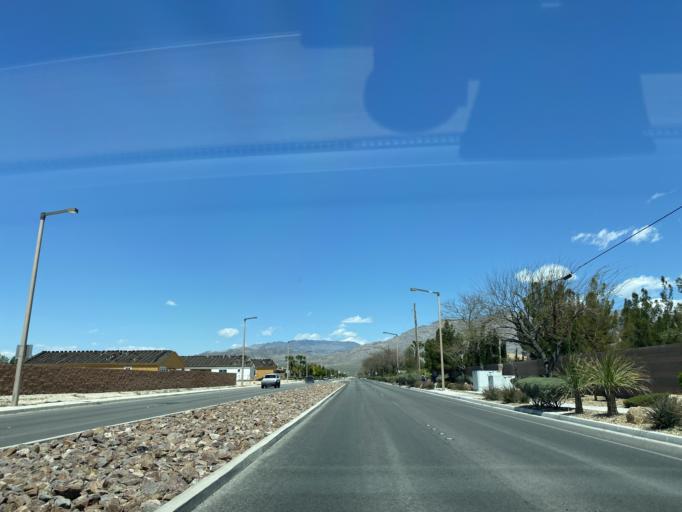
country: US
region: Nevada
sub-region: Clark County
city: North Las Vegas
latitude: 36.3088
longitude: -115.2241
